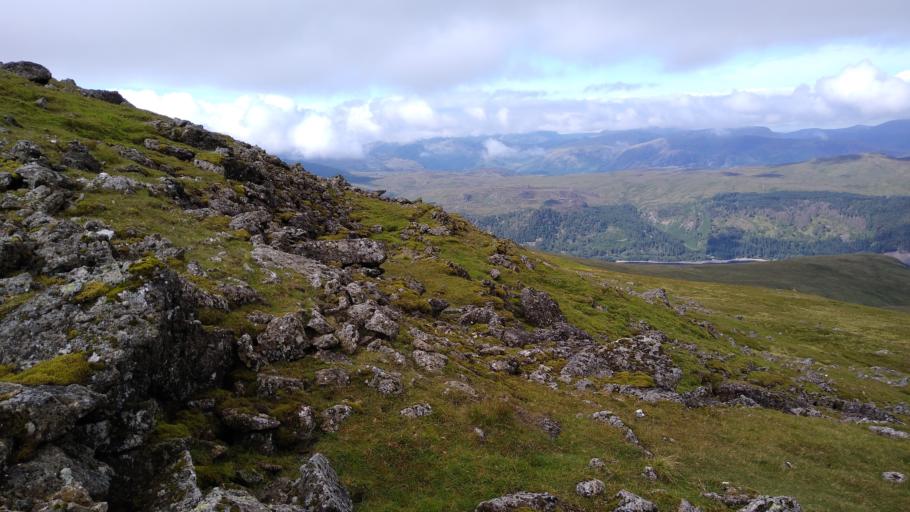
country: GB
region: England
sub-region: Cumbria
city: Keswick
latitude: 54.5482
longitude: -3.0178
